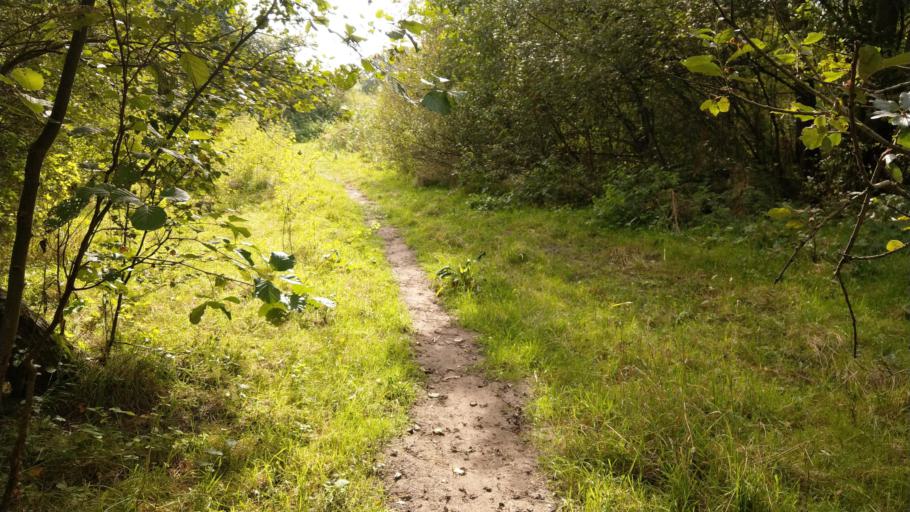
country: NL
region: North Brabant
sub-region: Gemeente Boxtel
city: Boxtel
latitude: 51.5837
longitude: 5.2880
